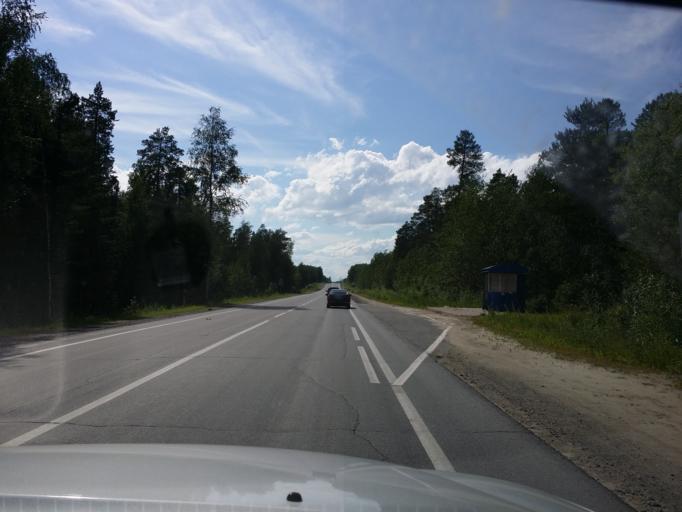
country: RU
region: Khanty-Mansiyskiy Avtonomnyy Okrug
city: Izluchinsk
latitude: 60.9653
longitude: 76.8170
